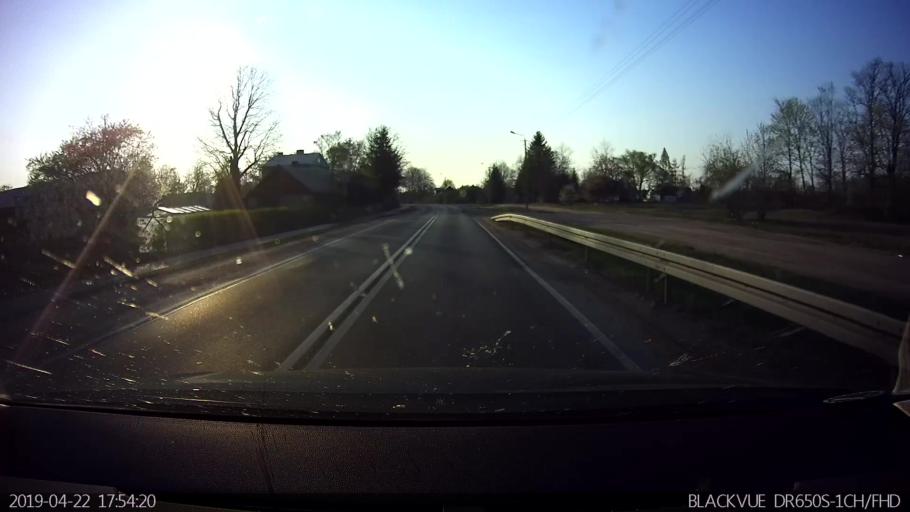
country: PL
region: Masovian Voivodeship
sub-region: Powiat wegrowski
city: Liw
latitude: 52.4567
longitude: 21.9412
